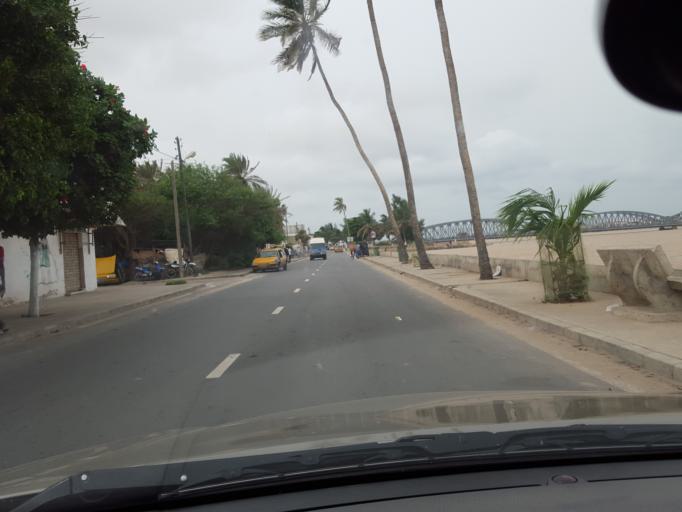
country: SN
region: Saint-Louis
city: Saint-Louis
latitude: 16.0279
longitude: -16.4973
